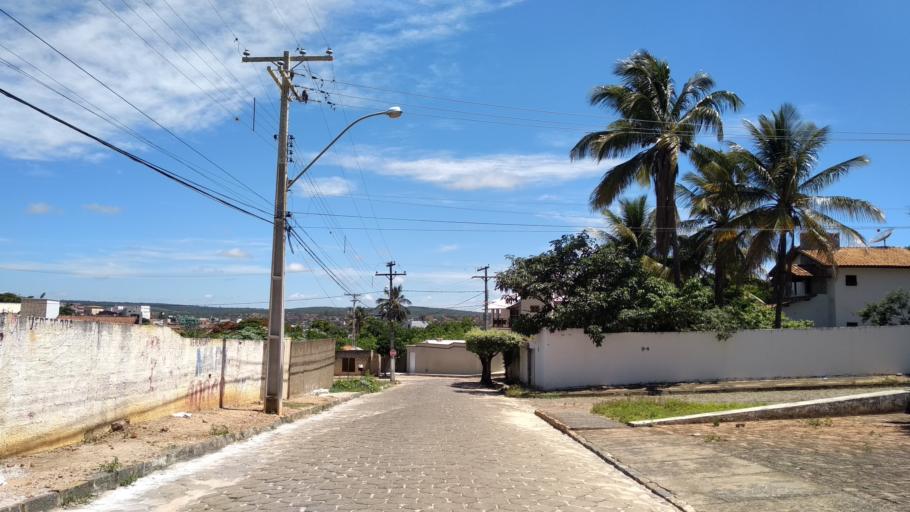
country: BR
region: Bahia
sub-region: Caetite
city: Caetite
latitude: -14.0715
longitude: -42.4817
